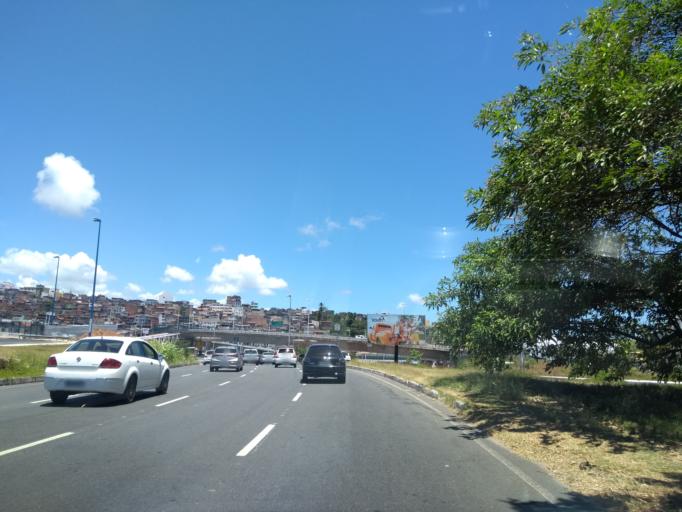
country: BR
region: Bahia
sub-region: Salvador
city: Salvador
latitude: -12.9775
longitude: -38.4612
